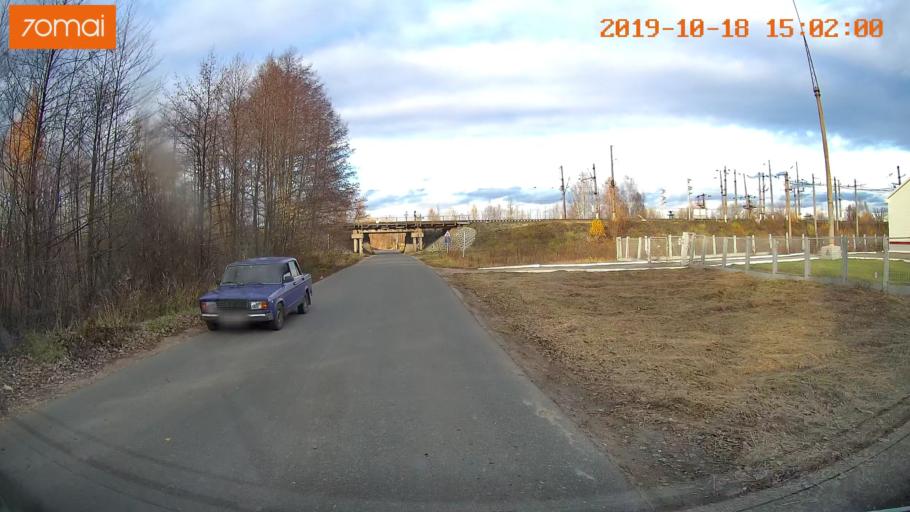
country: RU
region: Vladimir
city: Gus'-Khrustal'nyy
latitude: 55.5014
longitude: 40.6084
